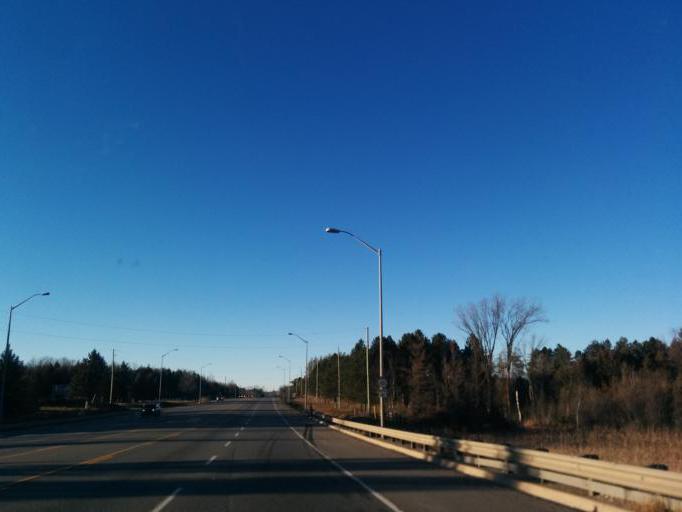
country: CA
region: Ontario
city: Orangeville
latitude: 43.9018
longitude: -80.0525
